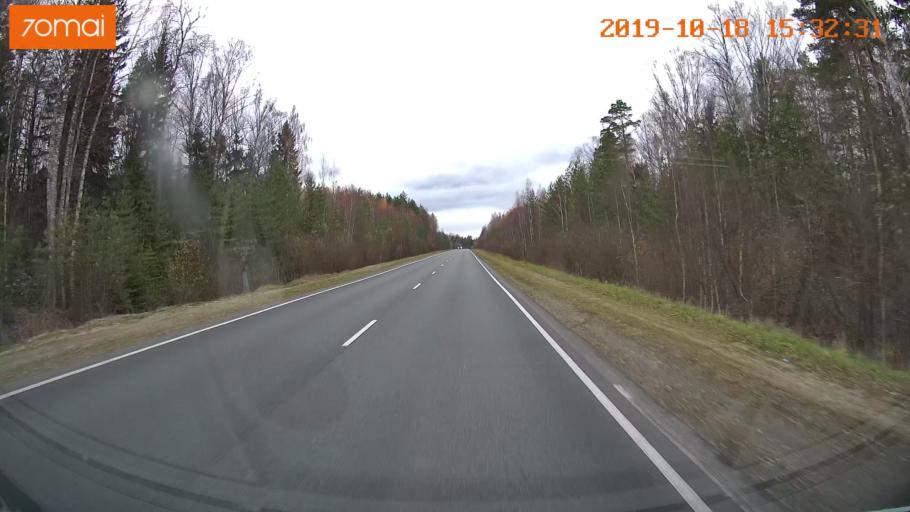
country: RU
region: Vladimir
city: Anopino
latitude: 55.8274
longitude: 40.6520
